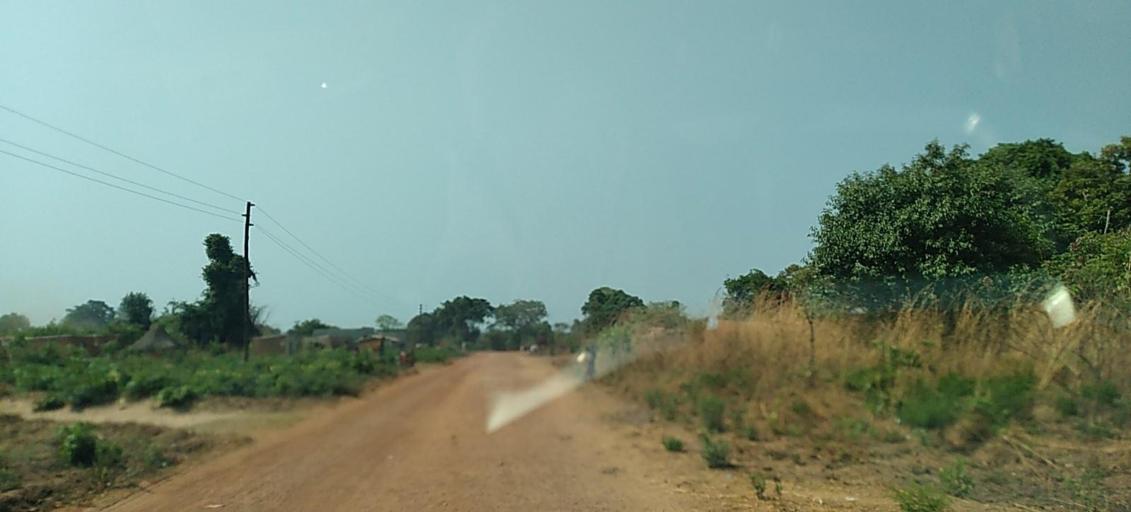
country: ZM
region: Copperbelt
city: Chingola
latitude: -12.9200
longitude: 27.3732
